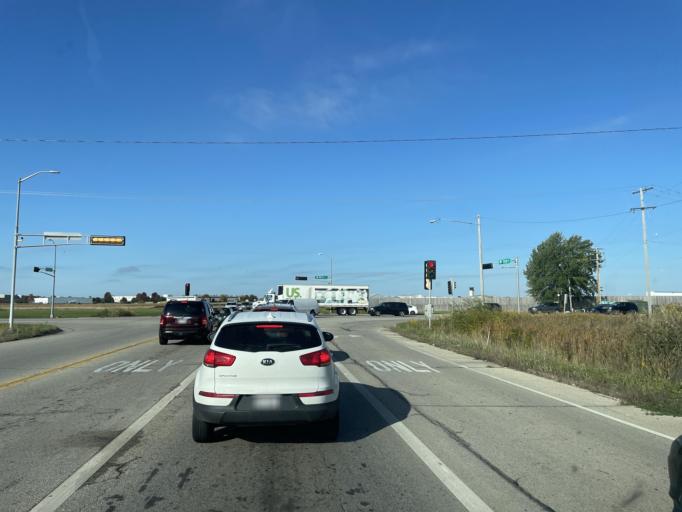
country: US
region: Wisconsin
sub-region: Kenosha County
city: Pleasant Prairie
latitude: 42.5892
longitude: -87.9142
